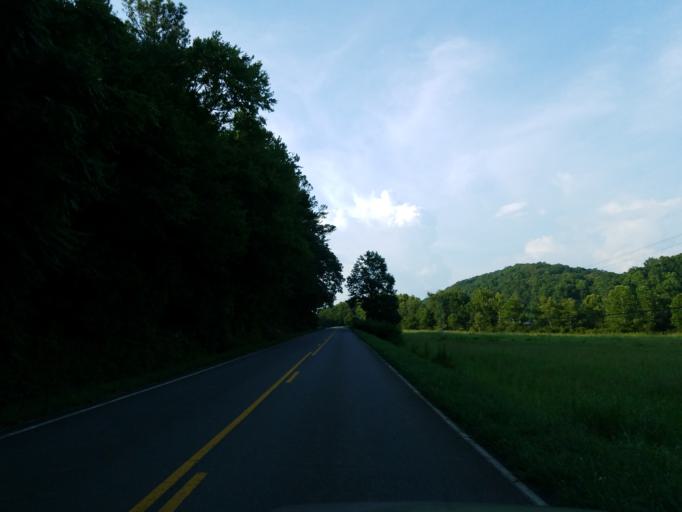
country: US
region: Georgia
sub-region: Pickens County
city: Jasper
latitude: 34.5544
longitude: -84.5397
